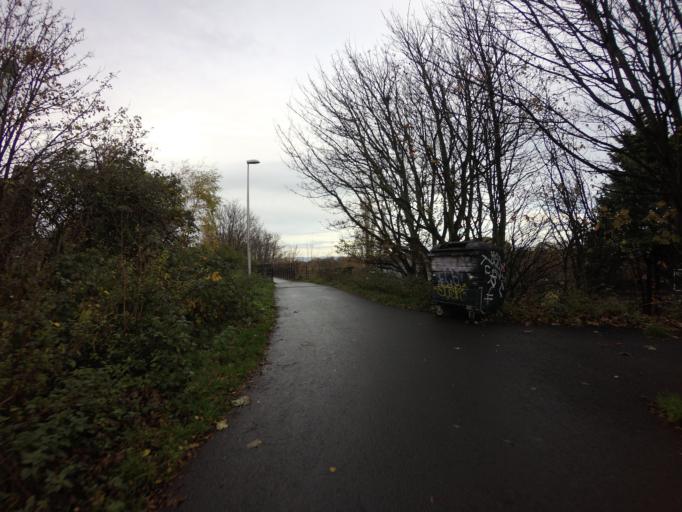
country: GB
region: Scotland
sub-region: West Lothian
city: Seafield
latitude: 55.9696
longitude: -3.1471
